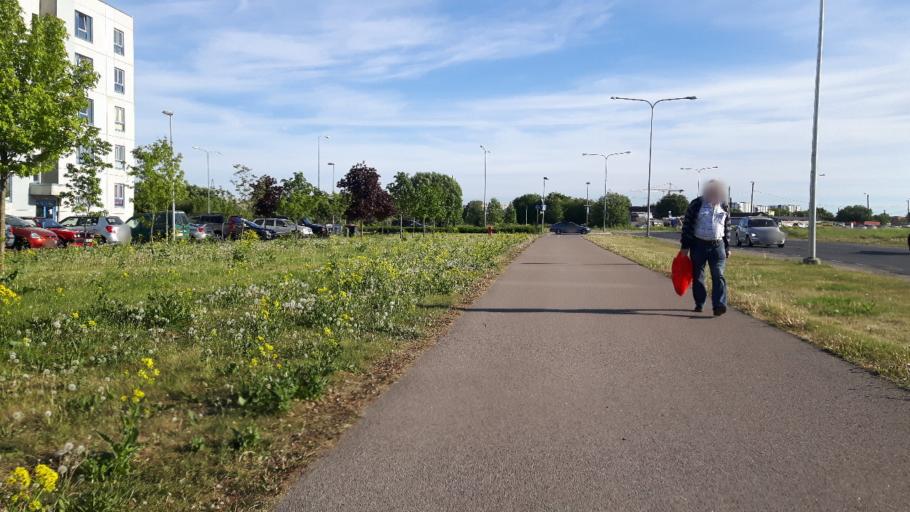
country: EE
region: Harju
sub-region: Tallinna linn
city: Kose
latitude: 59.4504
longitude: 24.8333
